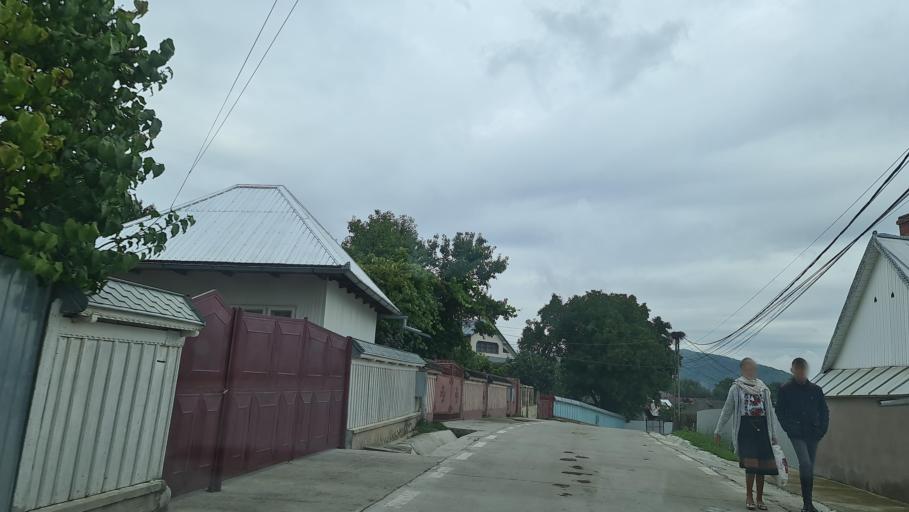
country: RO
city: Vanatori-Neamt
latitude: 47.2097
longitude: 26.3143
